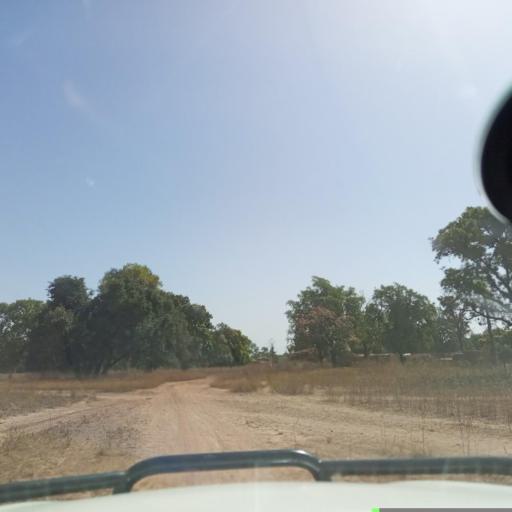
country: ML
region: Koulikoro
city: Dioila
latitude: 12.6242
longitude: -7.0253
